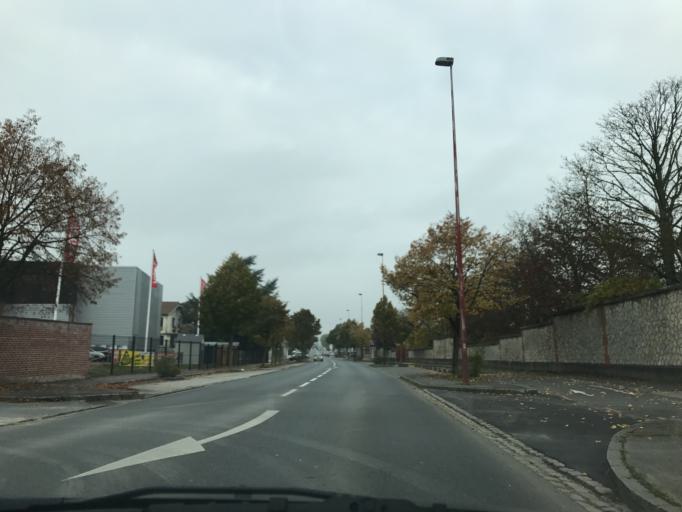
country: FR
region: Picardie
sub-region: Departement de la Somme
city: Peronne
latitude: 49.9142
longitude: 2.9340
